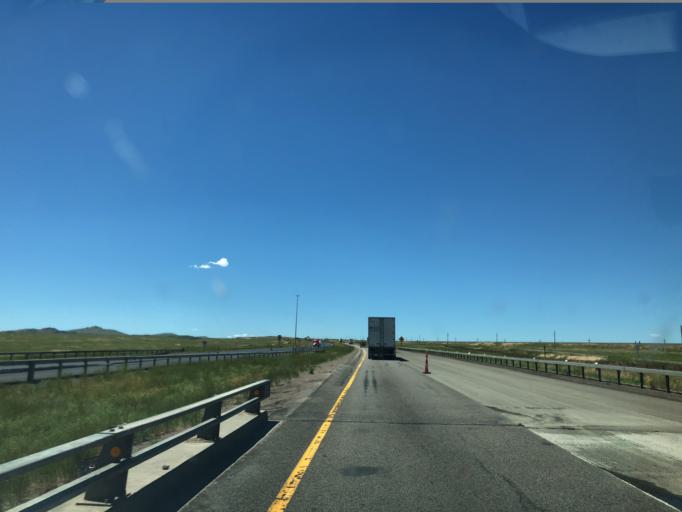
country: US
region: Wyoming
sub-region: Laramie County
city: Cheyenne
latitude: 41.0984
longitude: -105.1159
